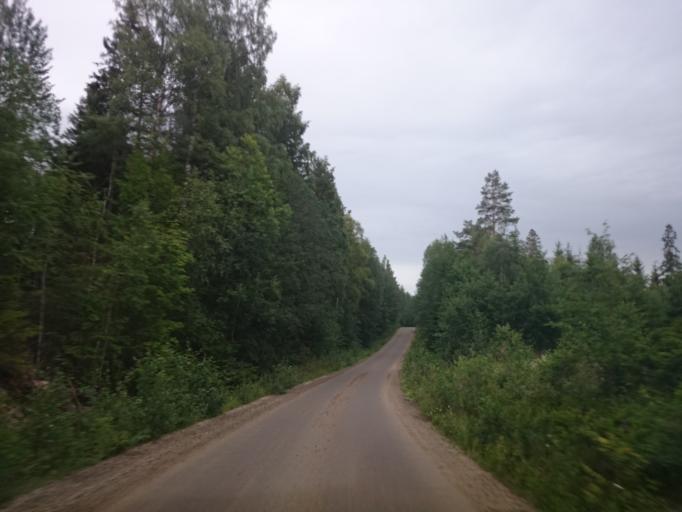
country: SE
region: Vaesternorrland
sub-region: Sundsvalls Kommun
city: Njurundabommen
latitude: 62.1408
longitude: 17.4140
